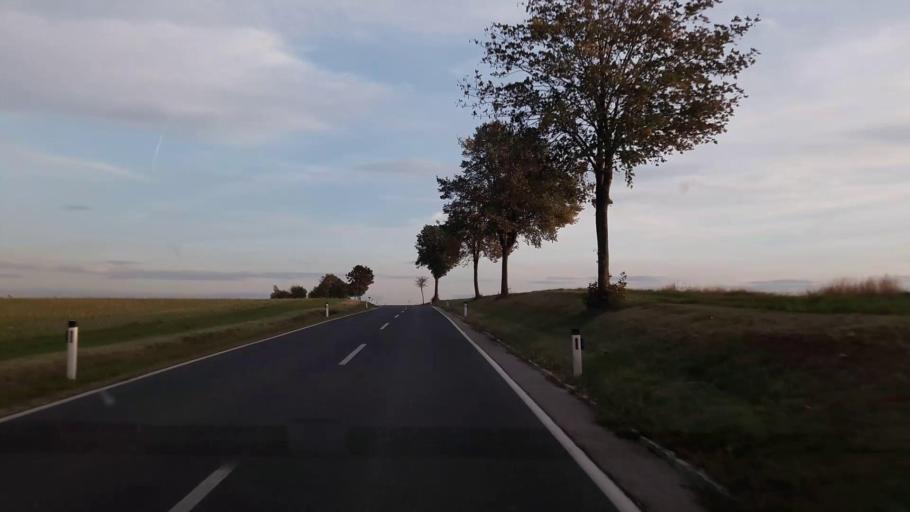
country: AT
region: Lower Austria
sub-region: Politischer Bezirk Korneuburg
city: Grossrussbach
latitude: 48.4412
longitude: 16.3893
